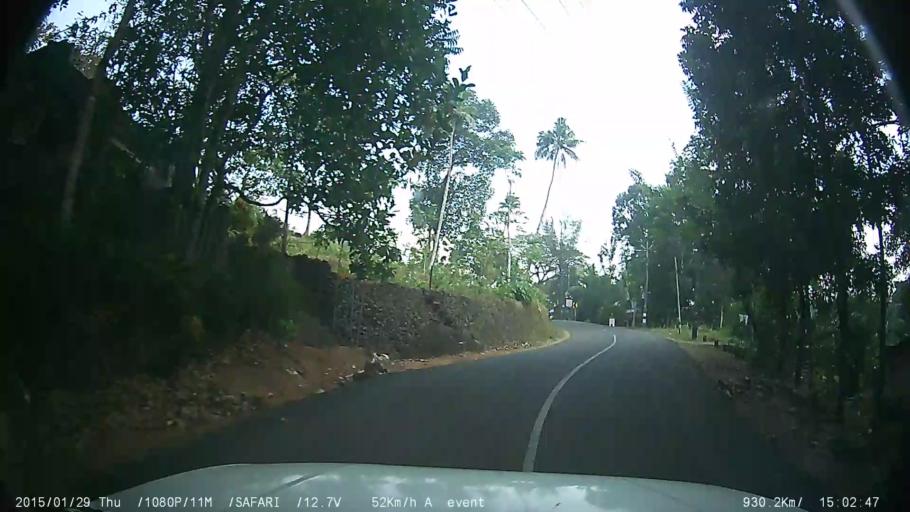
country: IN
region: Kerala
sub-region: Kottayam
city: Palackattumala
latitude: 9.7259
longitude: 76.5783
